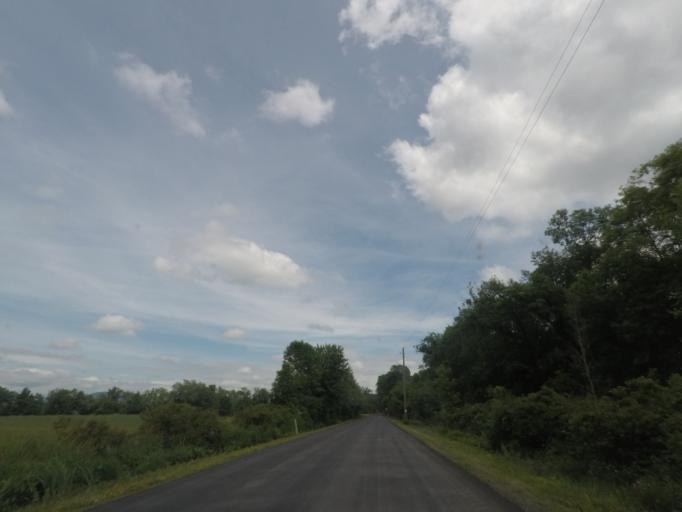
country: US
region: New York
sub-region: Saratoga County
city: Stillwater
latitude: 42.9903
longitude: -73.6134
